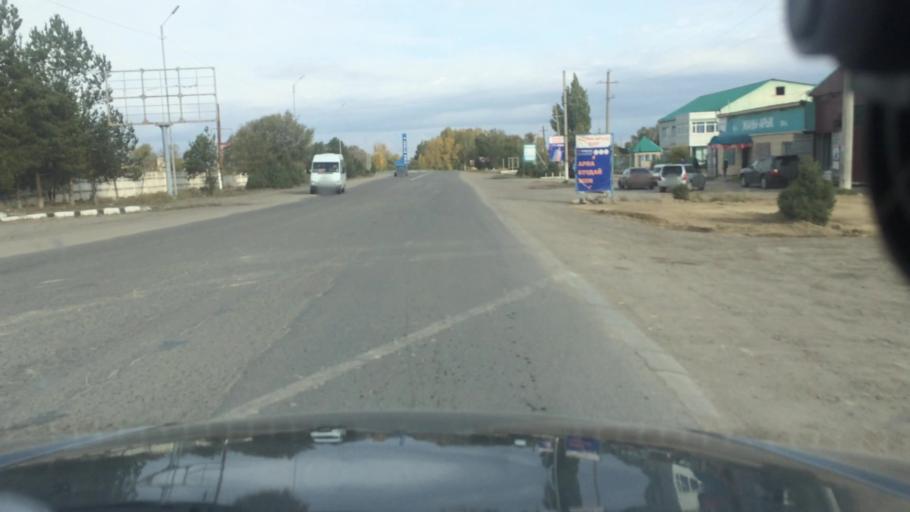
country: KG
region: Ysyk-Koel
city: Karakol
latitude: 42.5302
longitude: 78.3830
